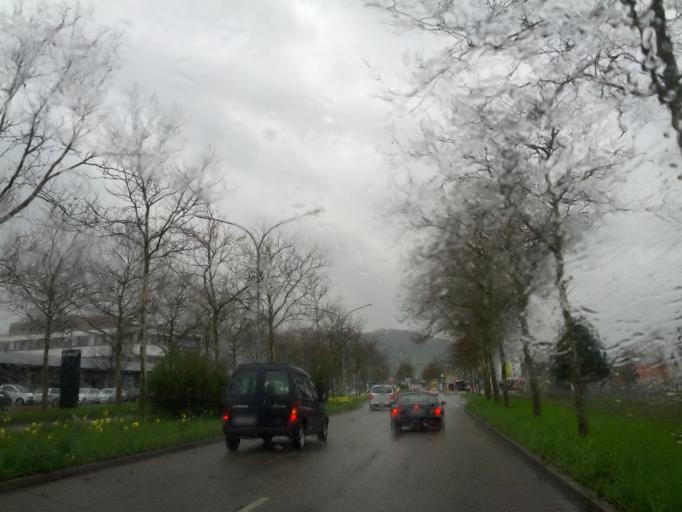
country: DE
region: Baden-Wuerttemberg
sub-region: Freiburg Region
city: Ebringen
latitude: 47.9905
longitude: 7.7973
